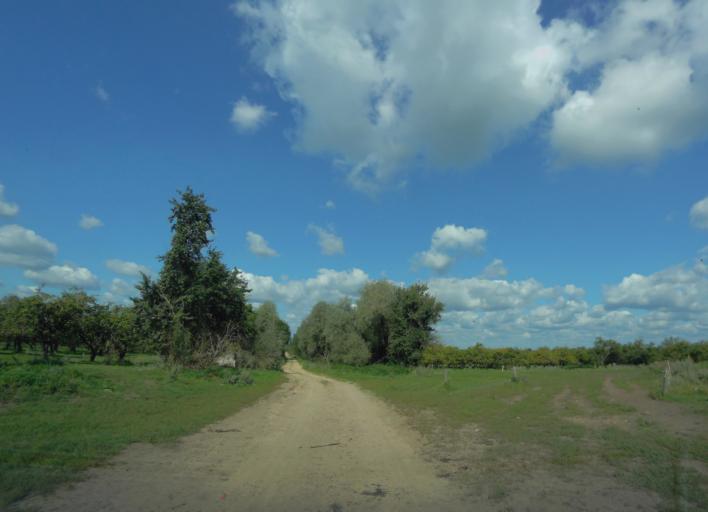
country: BY
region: Minsk
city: Zyembin
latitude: 54.4114
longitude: 28.3819
